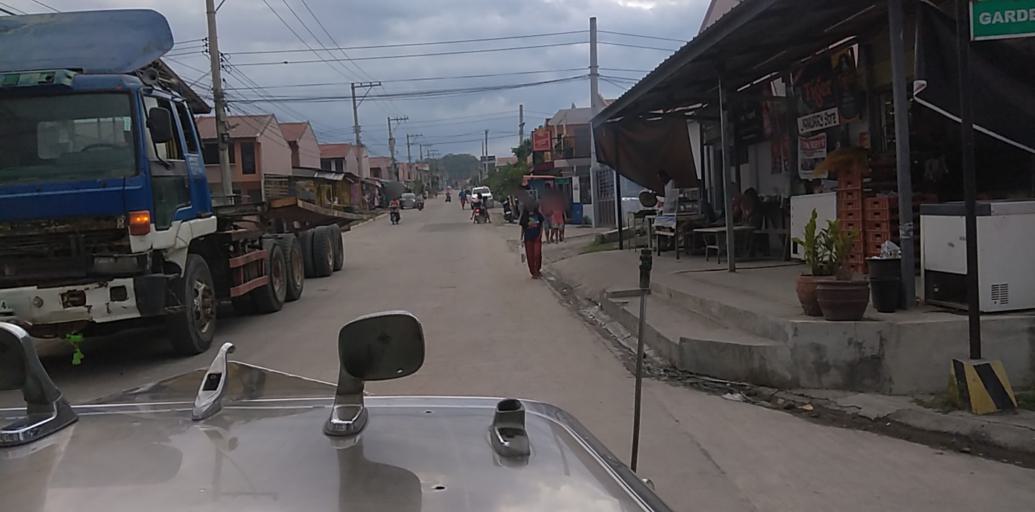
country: PH
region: Central Luzon
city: Santol
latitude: 15.1663
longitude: 120.5310
